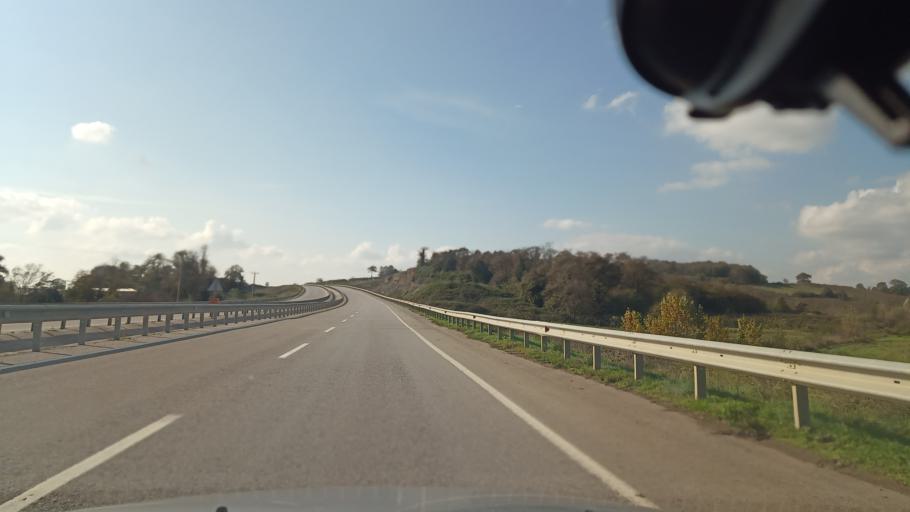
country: TR
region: Sakarya
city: Kaynarca
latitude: 41.0593
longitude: 30.3514
